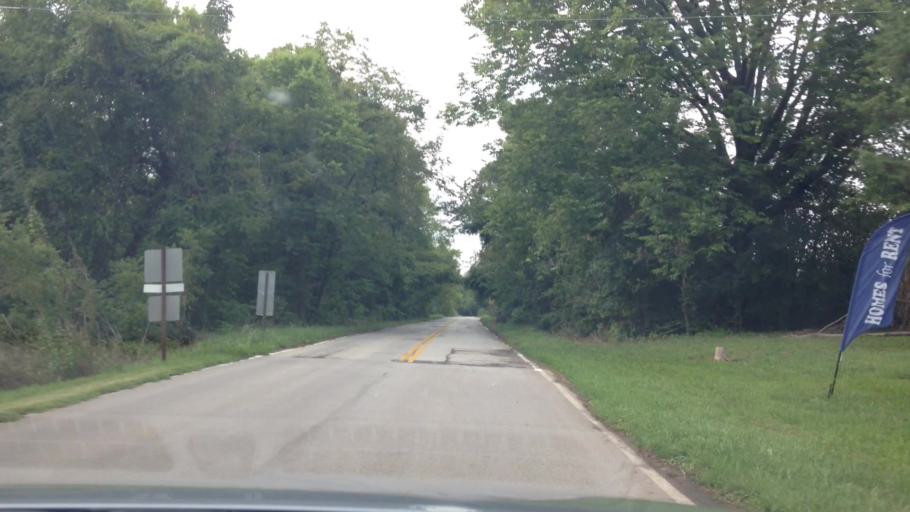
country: US
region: Missouri
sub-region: Platte County
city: Weatherby Lake
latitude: 39.3182
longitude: -94.6664
